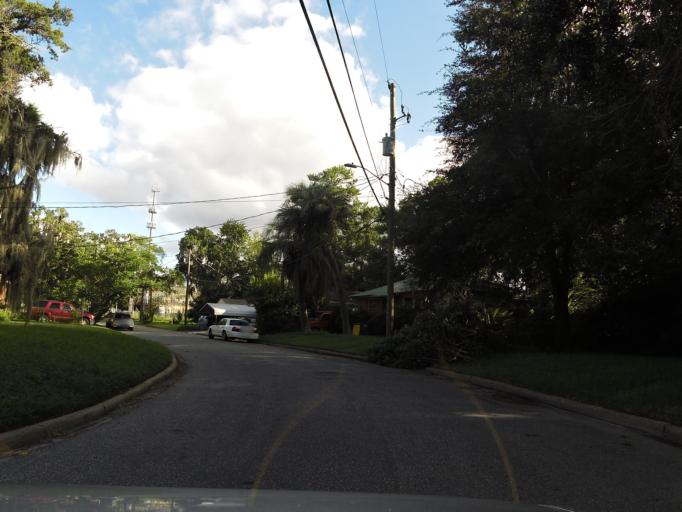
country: US
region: Florida
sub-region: Duval County
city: Jacksonville
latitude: 30.3124
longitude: -81.7083
